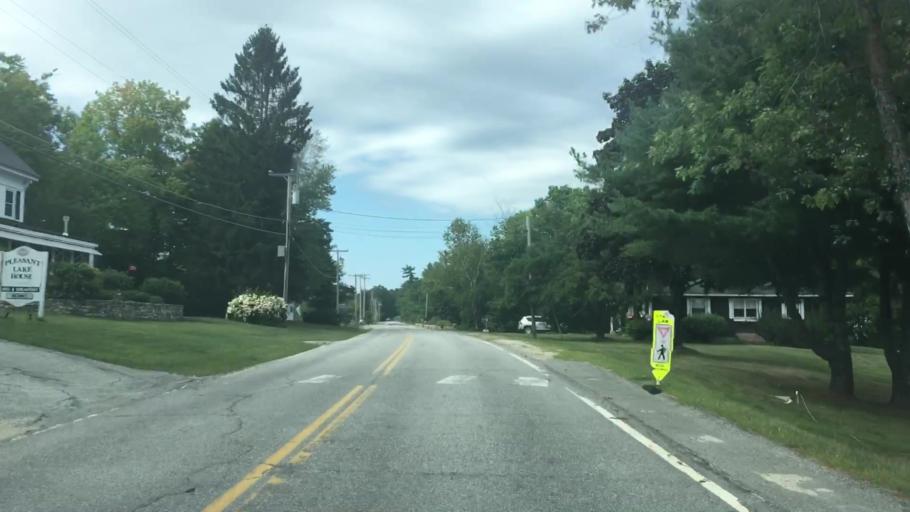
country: US
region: Maine
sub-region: Cumberland County
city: Raymond
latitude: 44.0098
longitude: -70.5233
